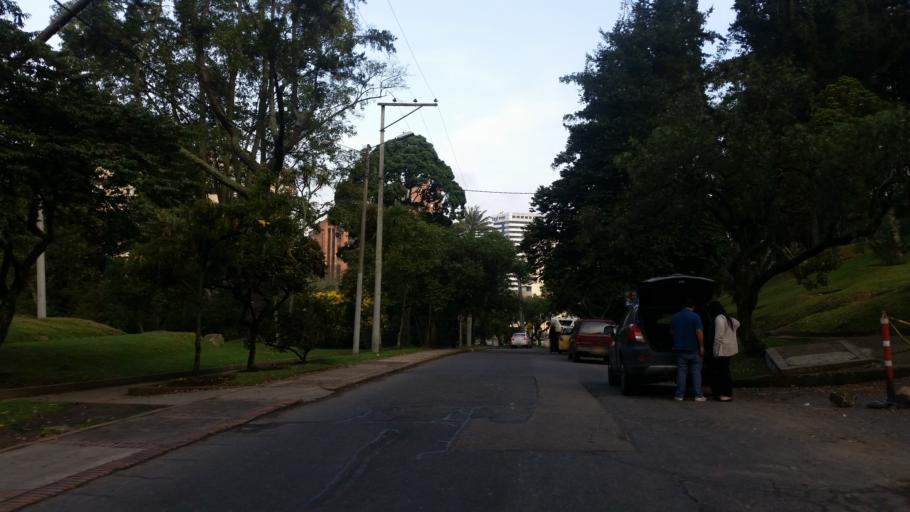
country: CO
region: Bogota D.C.
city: Bogota
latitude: 4.6249
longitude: -74.0647
